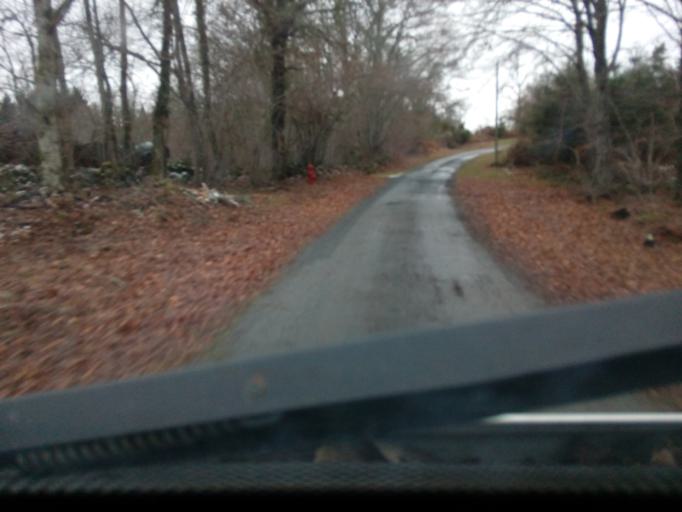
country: FR
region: Limousin
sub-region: Departement de la Creuse
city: Felletin
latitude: 45.8235
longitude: 2.2531
